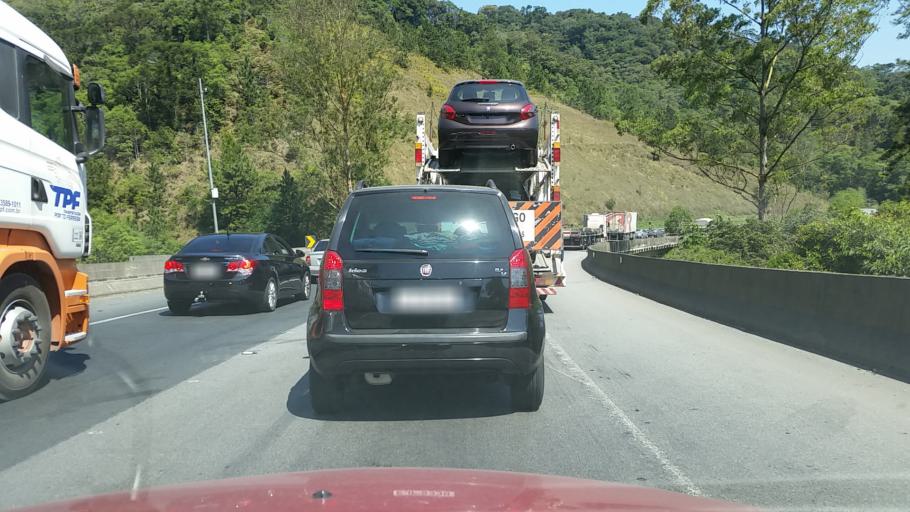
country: BR
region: Sao Paulo
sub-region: Juquitiba
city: Juquitiba
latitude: -24.0443
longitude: -47.1935
